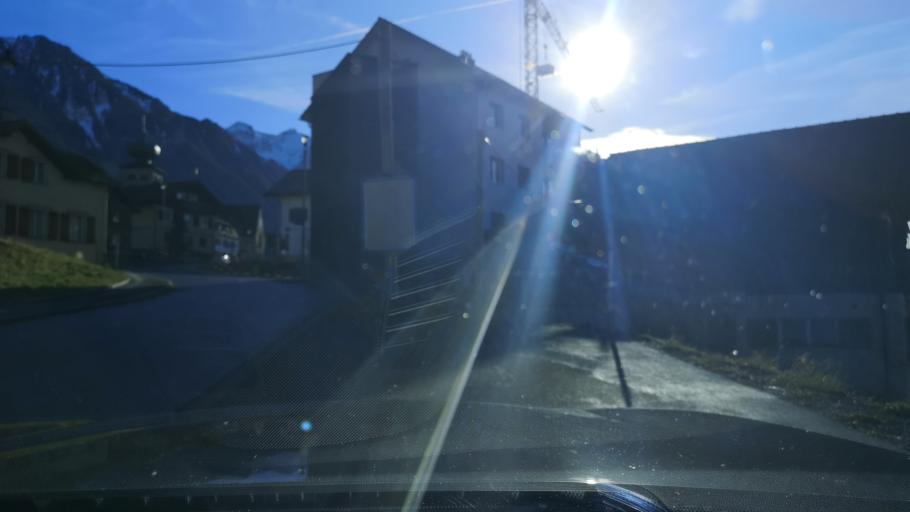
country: LI
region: Triesenberg
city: Triesenberg
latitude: 47.1194
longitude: 9.5427
